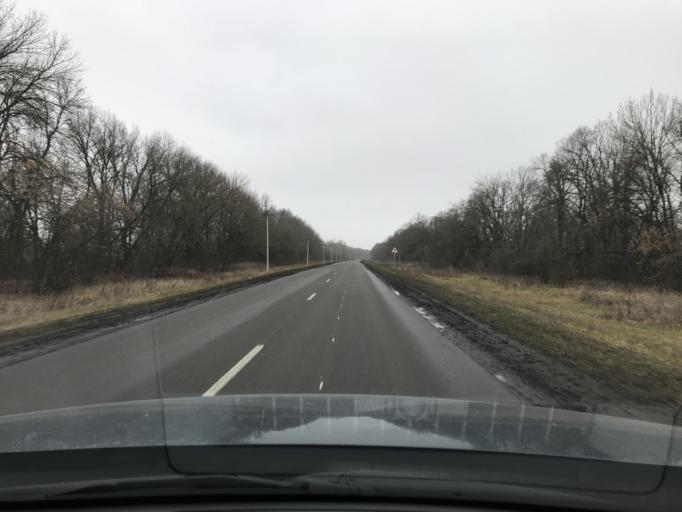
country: RU
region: Penza
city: Zemetchino
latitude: 53.5299
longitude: 42.6575
